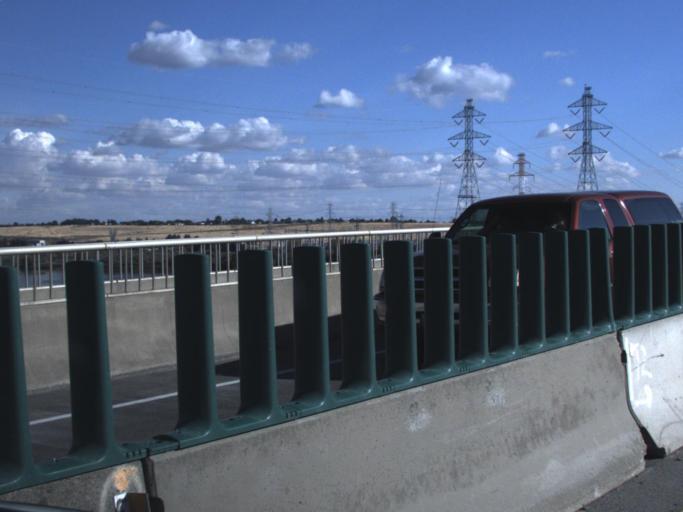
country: US
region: Oregon
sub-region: Umatilla County
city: Umatilla
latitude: 45.9330
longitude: -119.3294
